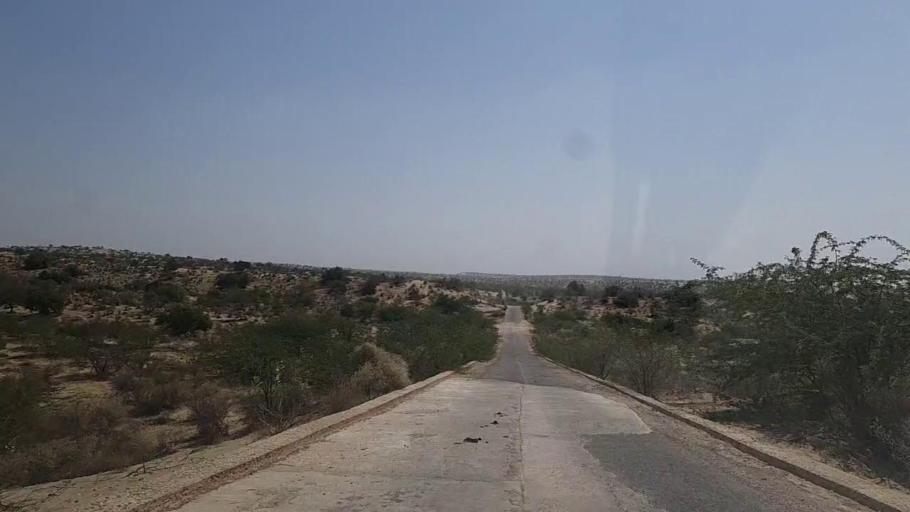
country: PK
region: Sindh
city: Diplo
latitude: 24.5018
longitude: 69.4277
